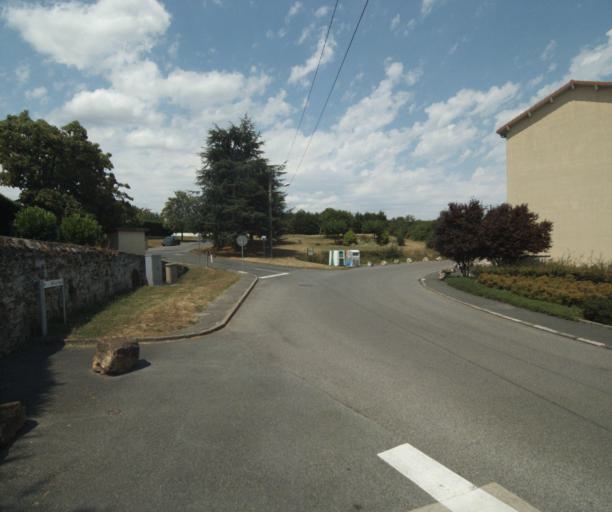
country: FR
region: Rhone-Alpes
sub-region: Departement du Rhone
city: Saint-Germain-Nuelles
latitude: 45.8403
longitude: 4.6201
